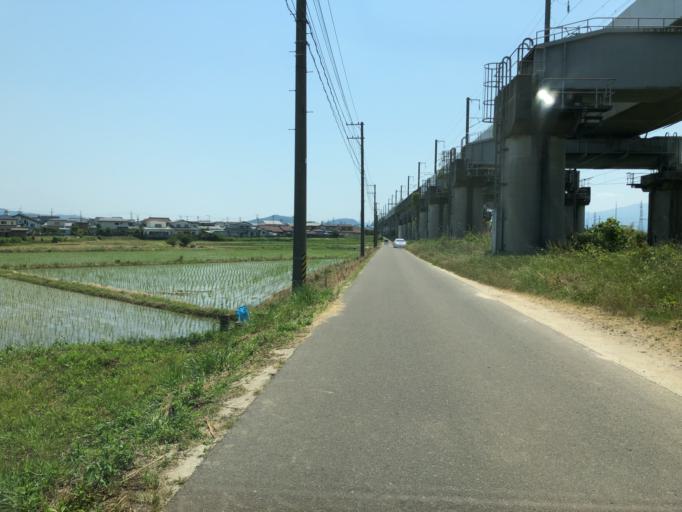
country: JP
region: Fukushima
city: Hobaramachi
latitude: 37.8290
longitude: 140.4972
